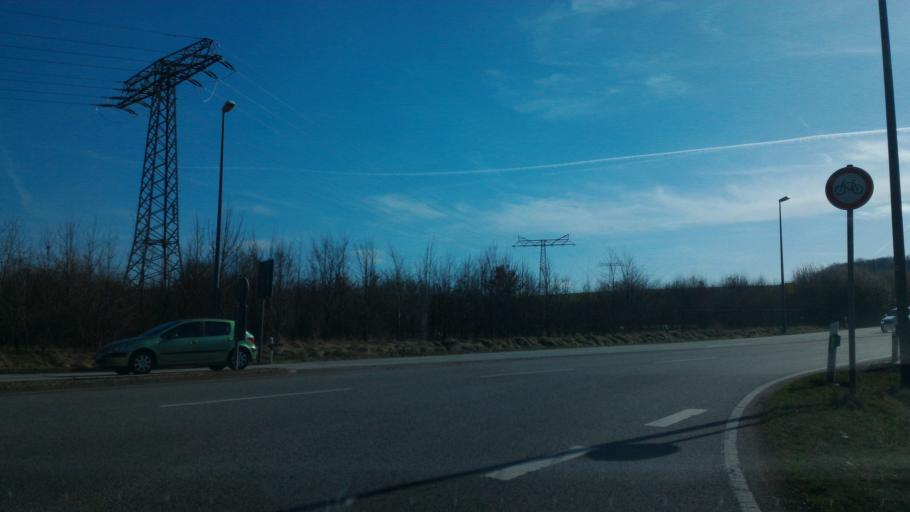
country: DE
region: Saxony
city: Dohna
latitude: 50.9871
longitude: 13.8166
